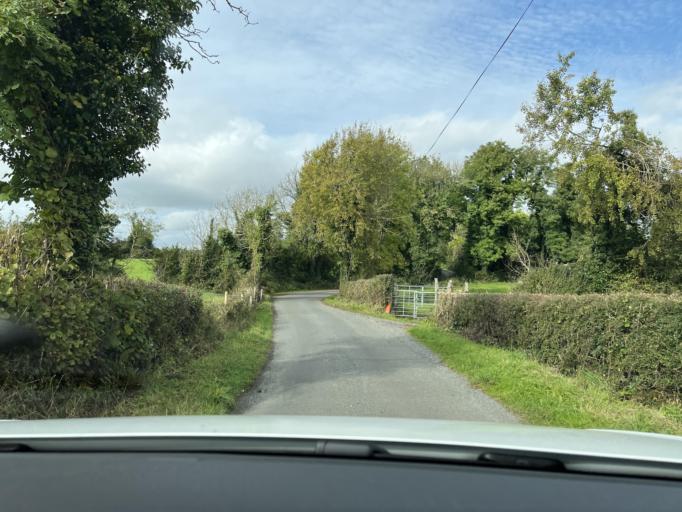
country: IE
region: Connaught
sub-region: County Leitrim
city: Carrick-on-Shannon
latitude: 53.9611
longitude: -8.0710
